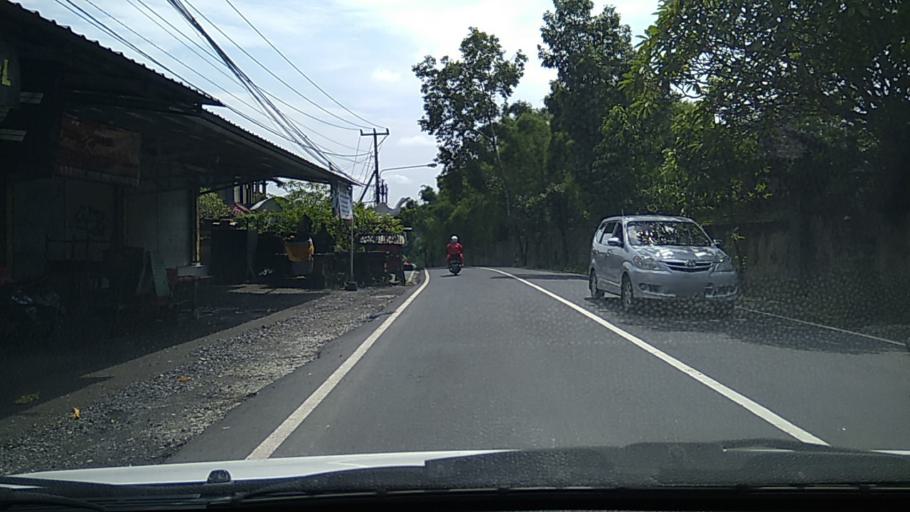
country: ID
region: Bali
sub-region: Kabupaten Gianyar
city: Ubud
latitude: -8.5228
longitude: 115.2808
